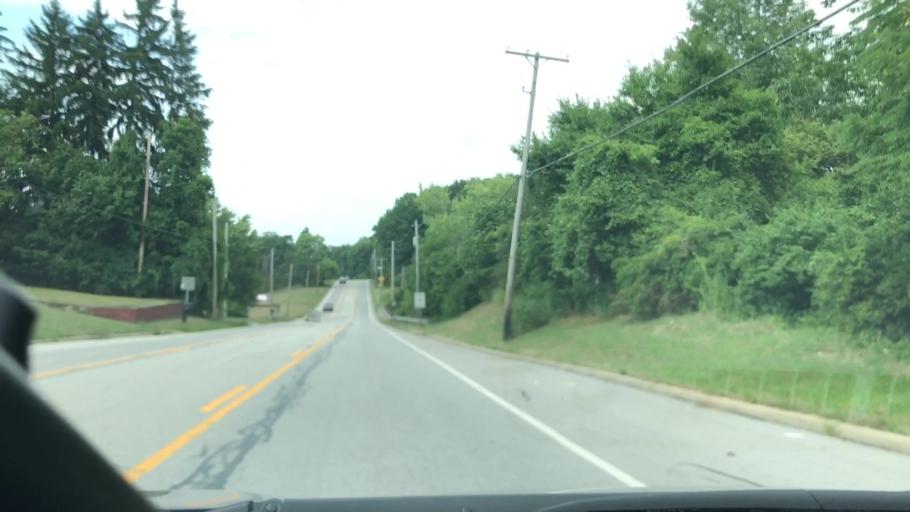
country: US
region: Ohio
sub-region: Summit County
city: Portage Lakes
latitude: 41.0132
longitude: -81.5236
